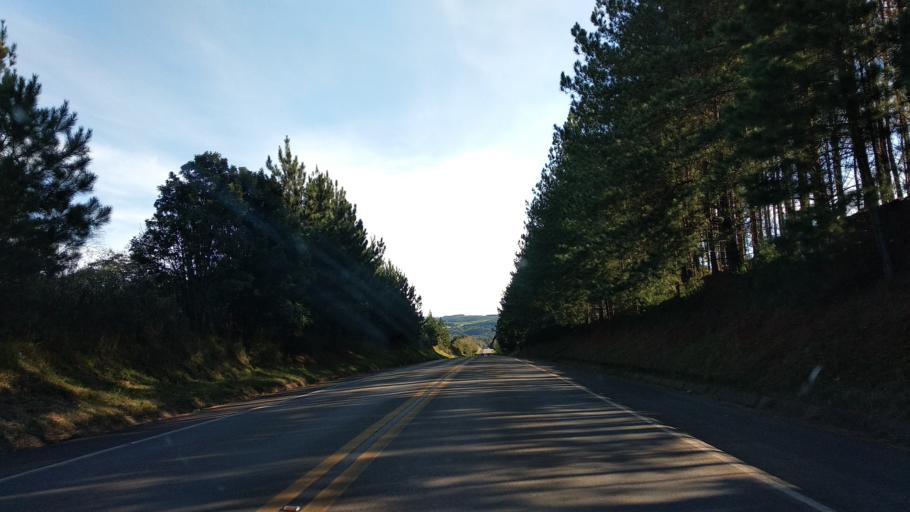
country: BR
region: Santa Catarina
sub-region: Celso Ramos
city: Celso Ramos
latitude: -27.5440
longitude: -51.4235
